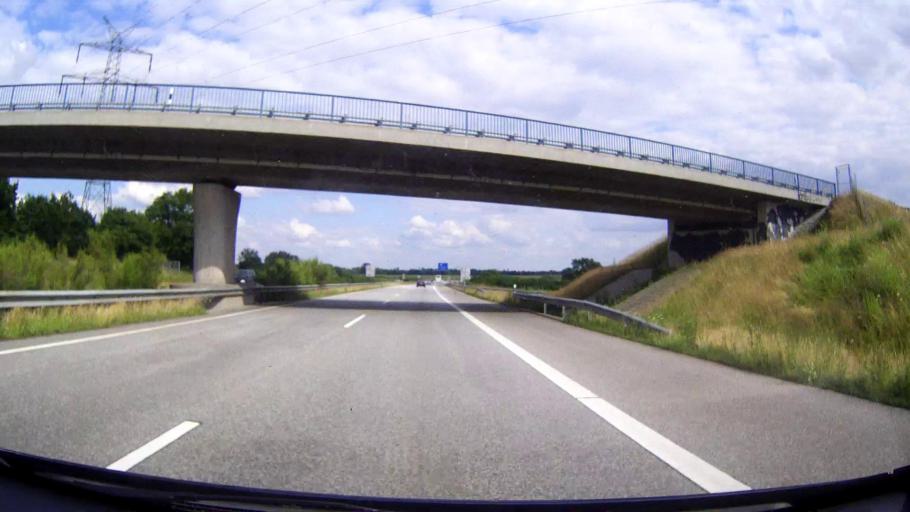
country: DE
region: Schleswig-Holstein
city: Monkhagen
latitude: 53.9109
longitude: 10.5528
